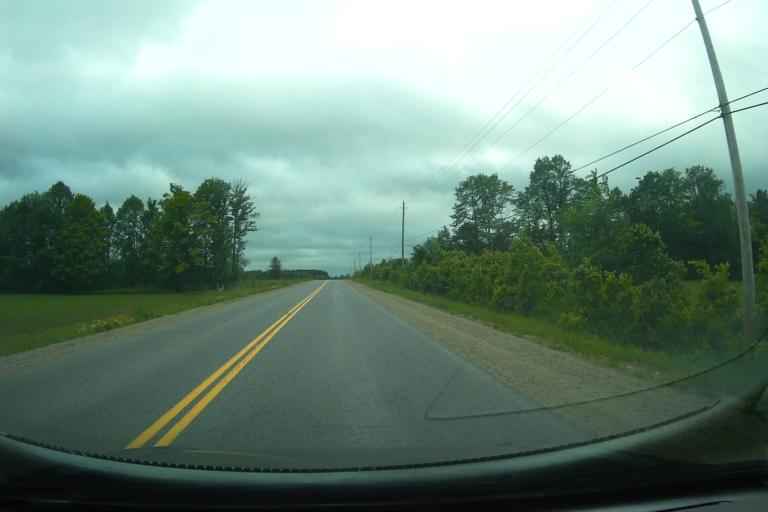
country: CA
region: Ontario
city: Pembroke
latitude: 45.5010
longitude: -77.1397
